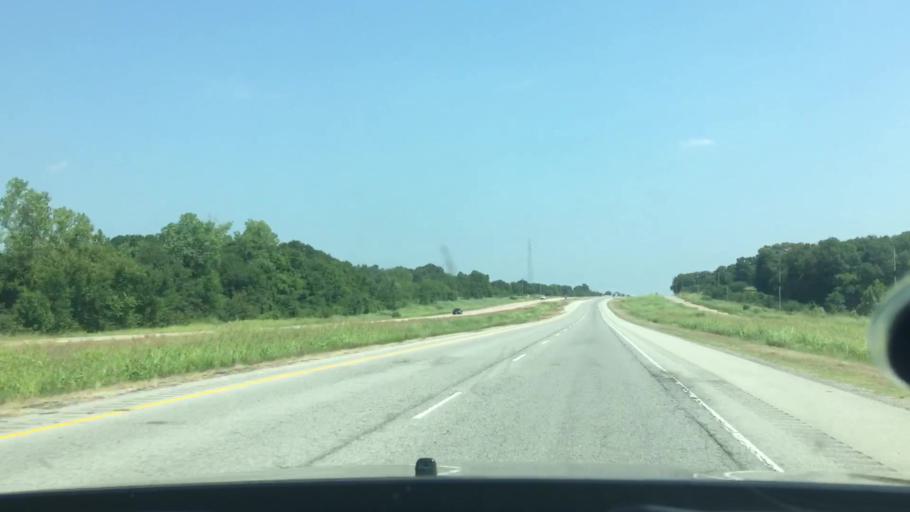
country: US
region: Oklahoma
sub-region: Atoka County
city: Atoka
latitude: 34.2617
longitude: -96.2103
